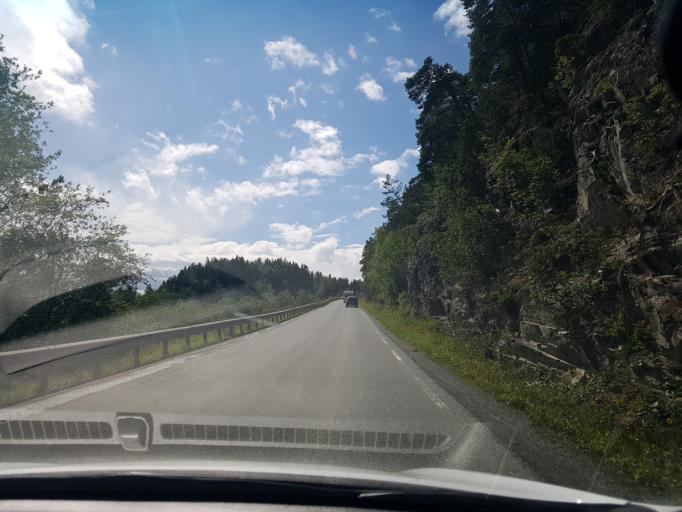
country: NO
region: Nord-Trondelag
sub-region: Frosta
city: Frosta
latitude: 63.5988
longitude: 10.8526
